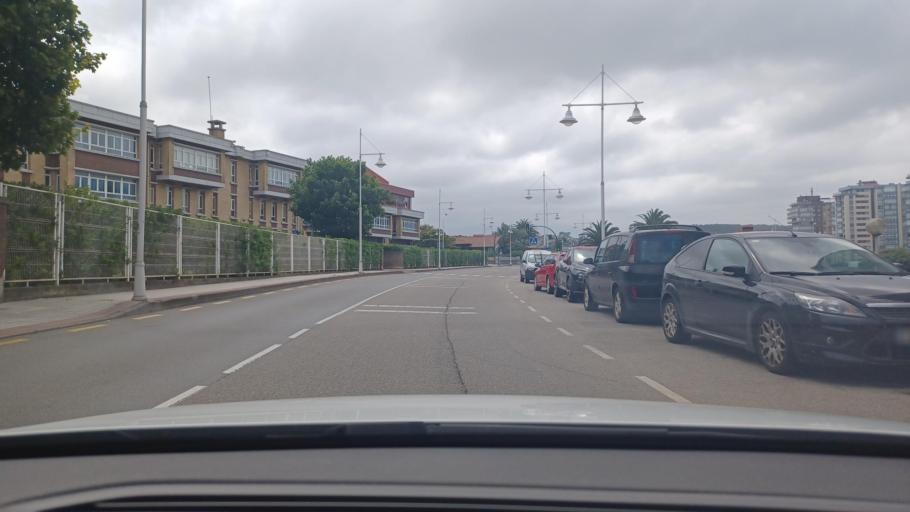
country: ES
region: Asturias
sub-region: Province of Asturias
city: Aviles
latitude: 43.5790
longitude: -5.9495
